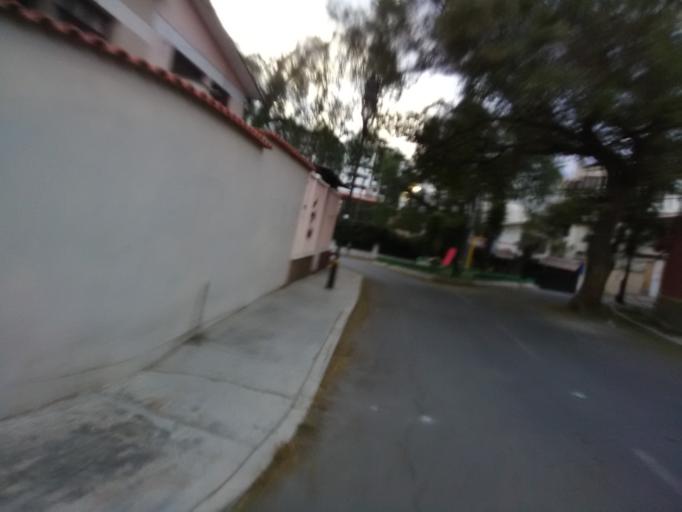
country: BO
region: Cochabamba
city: Cochabamba
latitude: -17.3755
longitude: -66.1416
